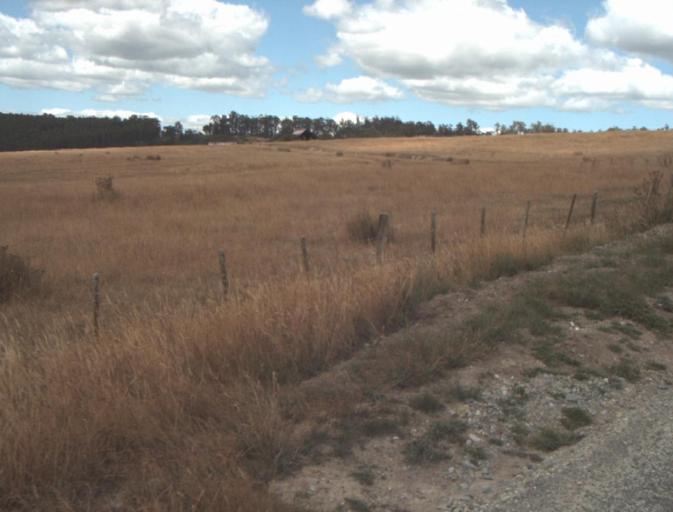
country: AU
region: Tasmania
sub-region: Launceston
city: Mayfield
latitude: -41.1931
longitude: 147.1730
